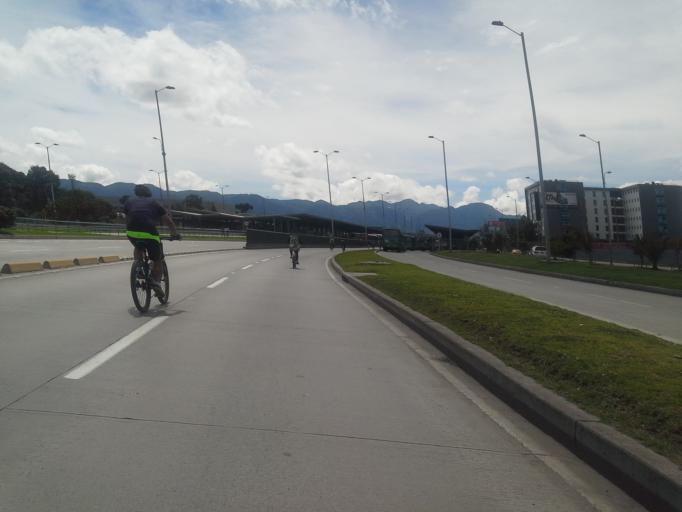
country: CO
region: Bogota D.C.
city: Bogota
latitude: 4.6832
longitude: -74.1231
